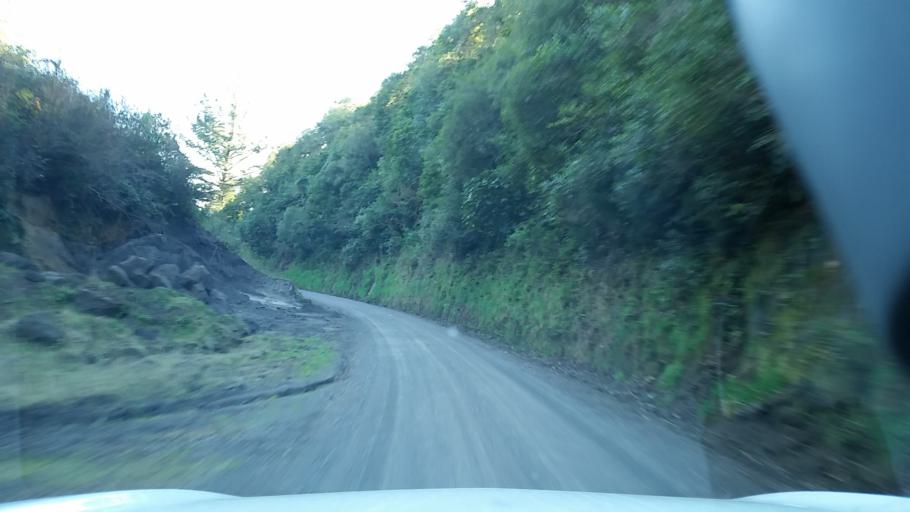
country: NZ
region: Waikato
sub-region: Taupo District
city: Taupo
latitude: -38.4376
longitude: 176.1674
